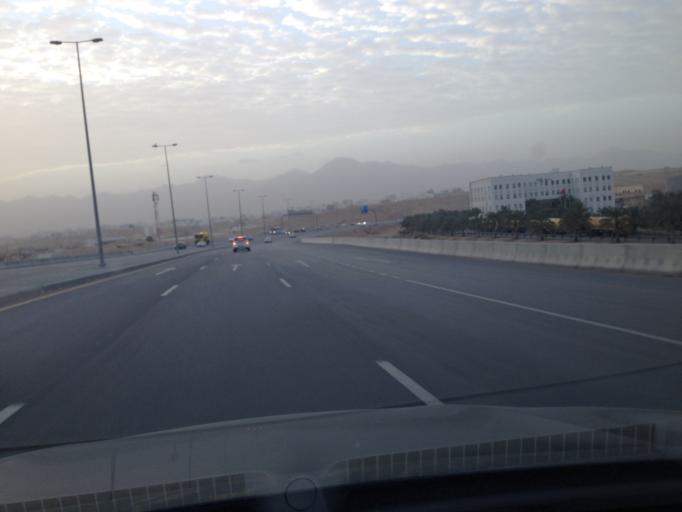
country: OM
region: Muhafazat Masqat
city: Bawshar
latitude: 23.5679
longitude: 58.3360
